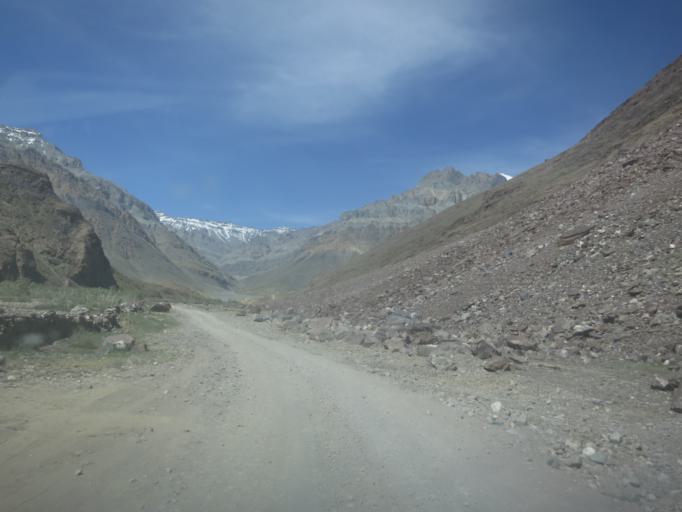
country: IN
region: Himachal Pradesh
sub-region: Kulu
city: Manali
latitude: 32.4406
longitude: 77.6852
